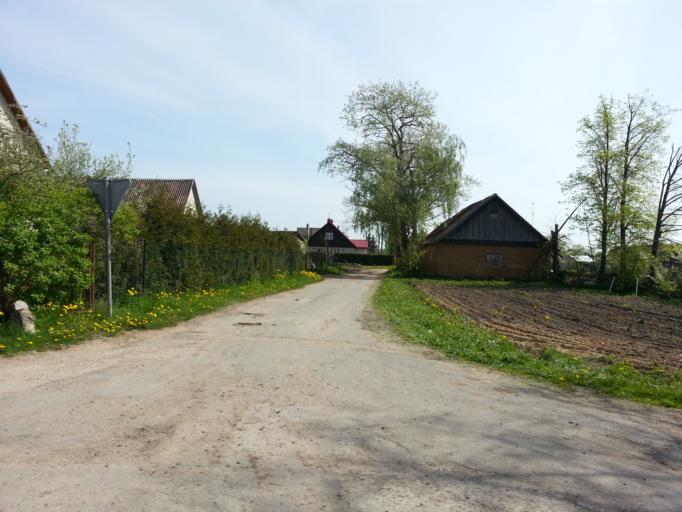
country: LT
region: Panevezys
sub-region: Panevezys City
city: Panevezys
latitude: 55.8294
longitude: 24.2552
